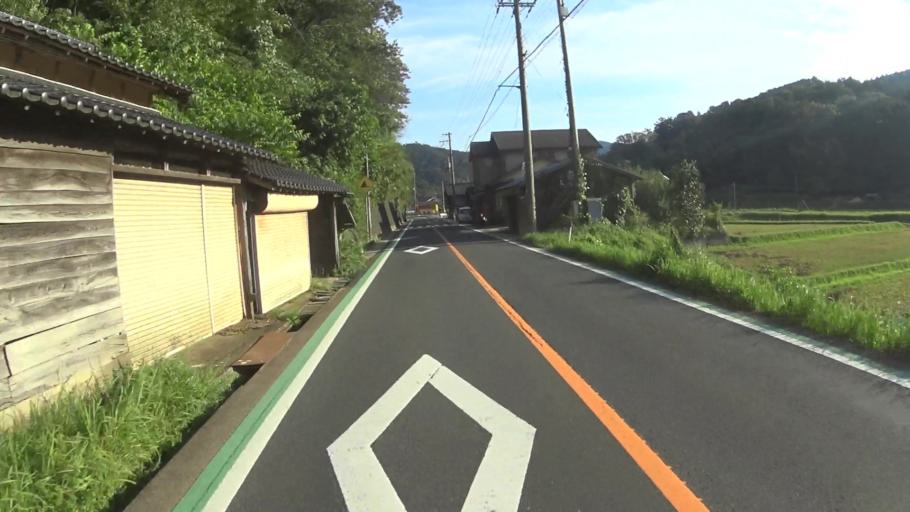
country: JP
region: Hyogo
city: Toyooka
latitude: 35.5961
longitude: 134.9054
